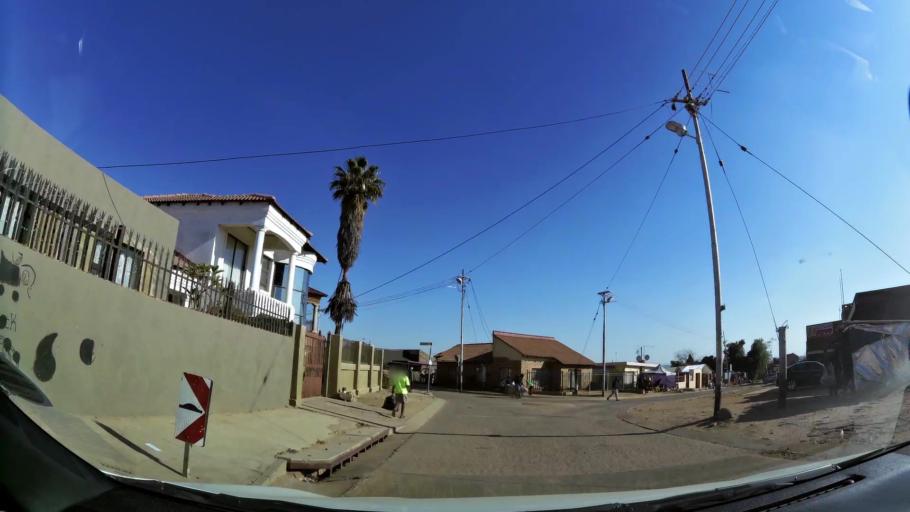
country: ZA
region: Gauteng
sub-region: City of Tshwane Metropolitan Municipality
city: Cullinan
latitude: -25.7167
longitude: 28.3813
